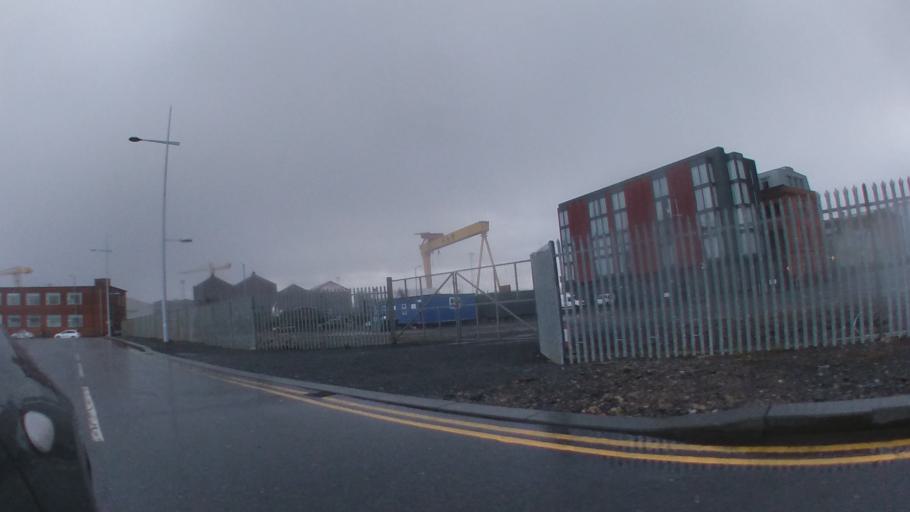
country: GB
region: Northern Ireland
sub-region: City of Belfast
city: Belfast
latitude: 54.6084
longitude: -5.9094
